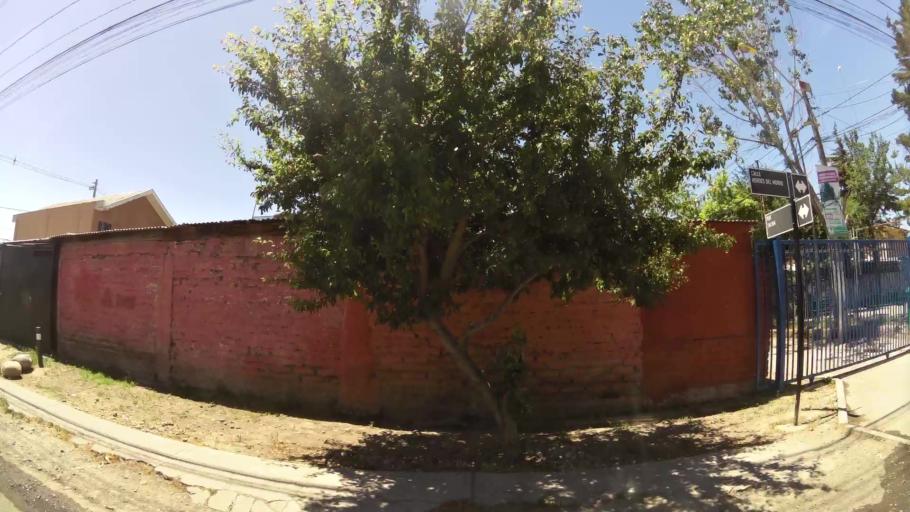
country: CL
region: Santiago Metropolitan
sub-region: Provincia de Maipo
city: San Bernardo
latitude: -33.5752
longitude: -70.6695
